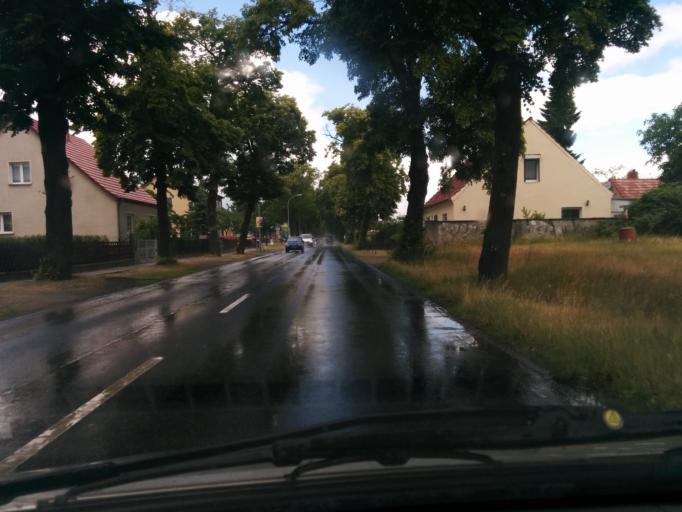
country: DE
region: Brandenburg
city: Falkensee
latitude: 52.5627
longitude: 13.1191
